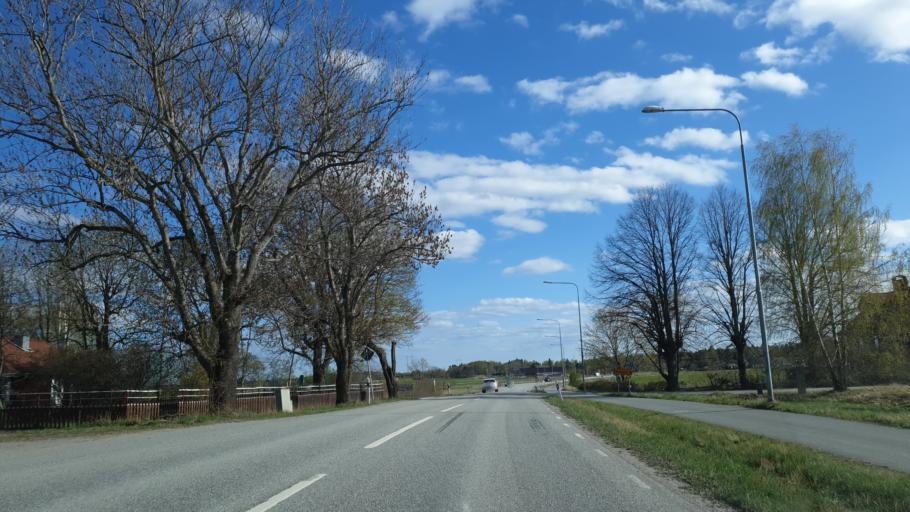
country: SE
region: Stockholm
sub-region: Sigtuna Kommun
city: Rosersberg
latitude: 59.5938
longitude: 17.8897
